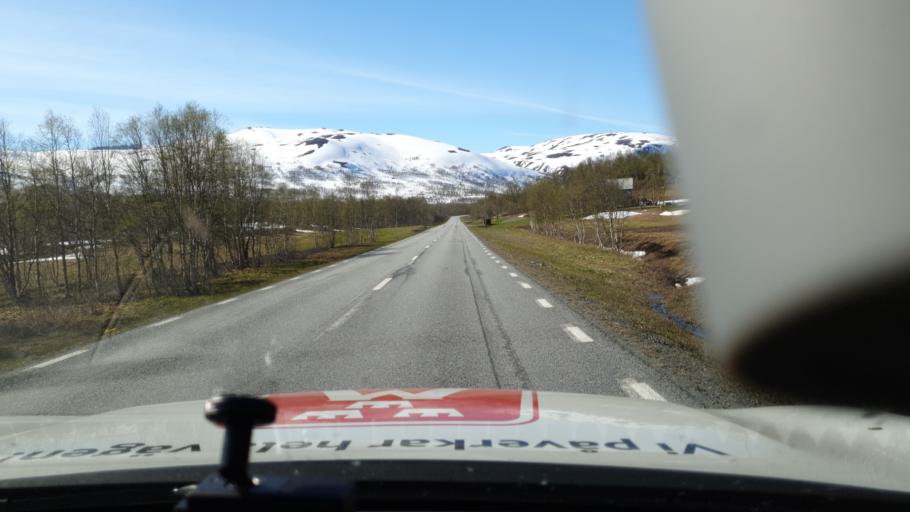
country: NO
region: Nordland
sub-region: Rana
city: Mo i Rana
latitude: 65.8775
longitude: 15.0016
